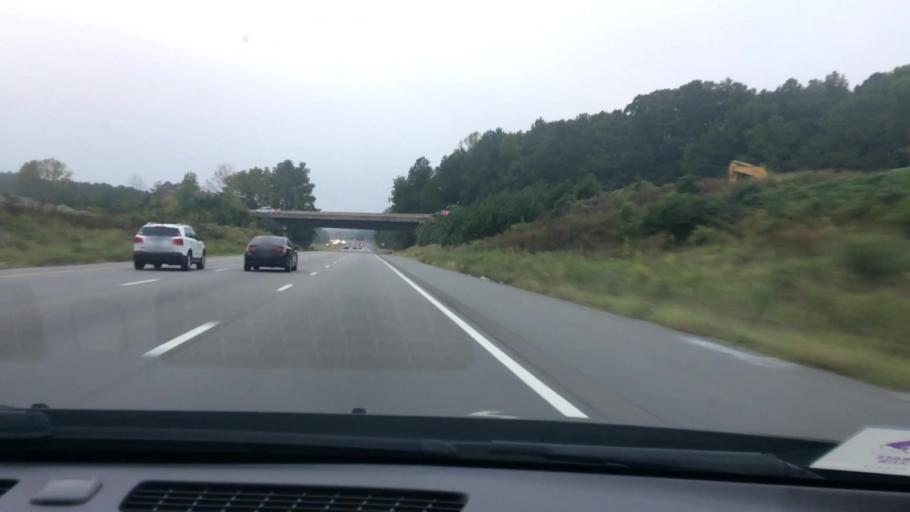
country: US
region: North Carolina
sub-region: Wake County
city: Garner
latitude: 35.7543
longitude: -78.5925
